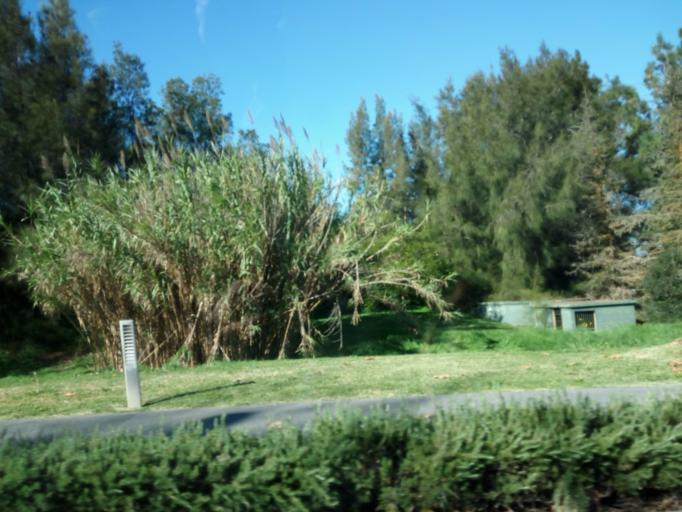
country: PT
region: Faro
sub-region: Loule
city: Vilamoura
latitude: 37.1017
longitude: -8.1251
